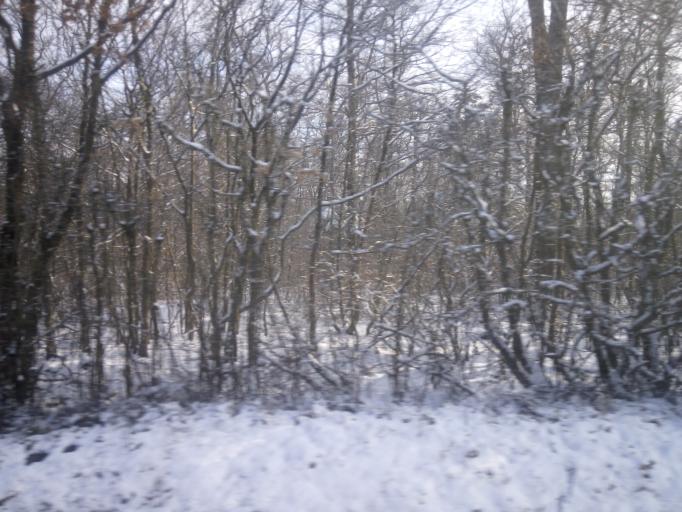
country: LU
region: Grevenmacher
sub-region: Canton d'Echternach
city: Consdorf
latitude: 49.7640
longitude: 6.3370
